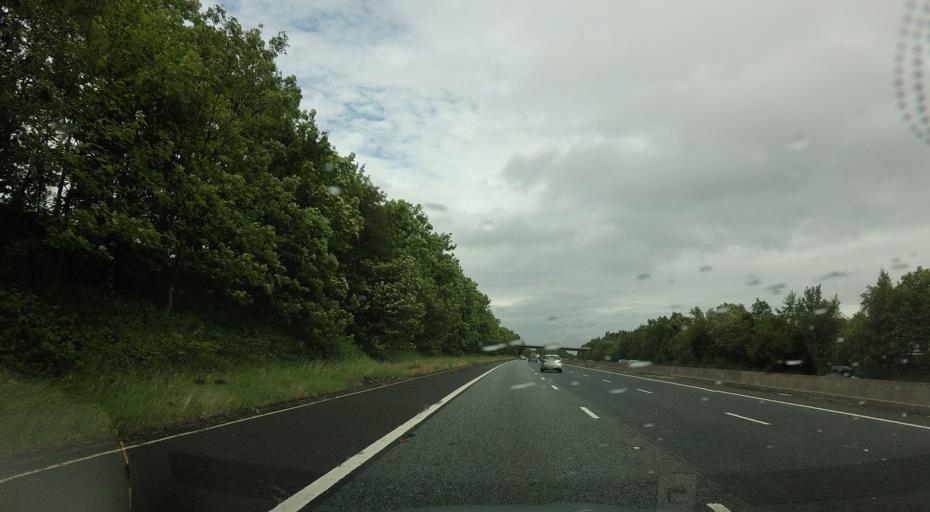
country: GB
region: England
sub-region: Cumbria
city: Scotby
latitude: 54.8237
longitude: -2.8887
